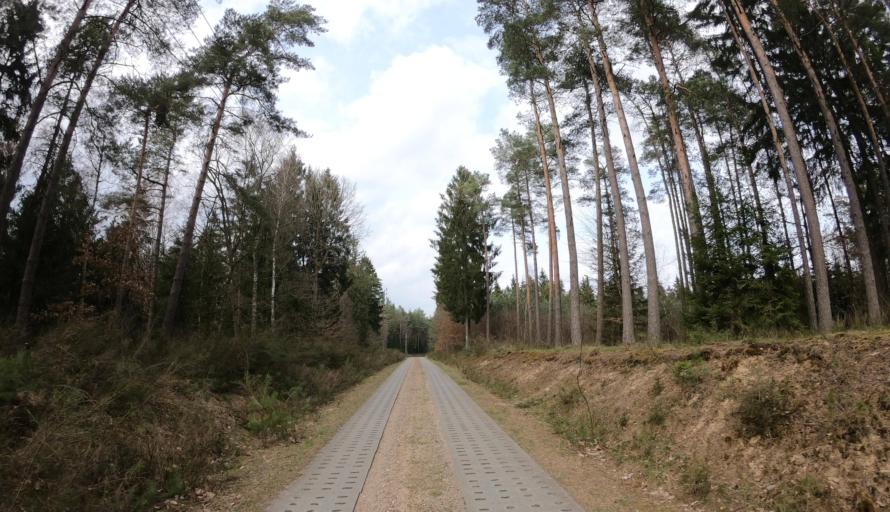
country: PL
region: West Pomeranian Voivodeship
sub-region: Powiat swidwinski
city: Rabino
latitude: 53.8664
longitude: 15.8718
